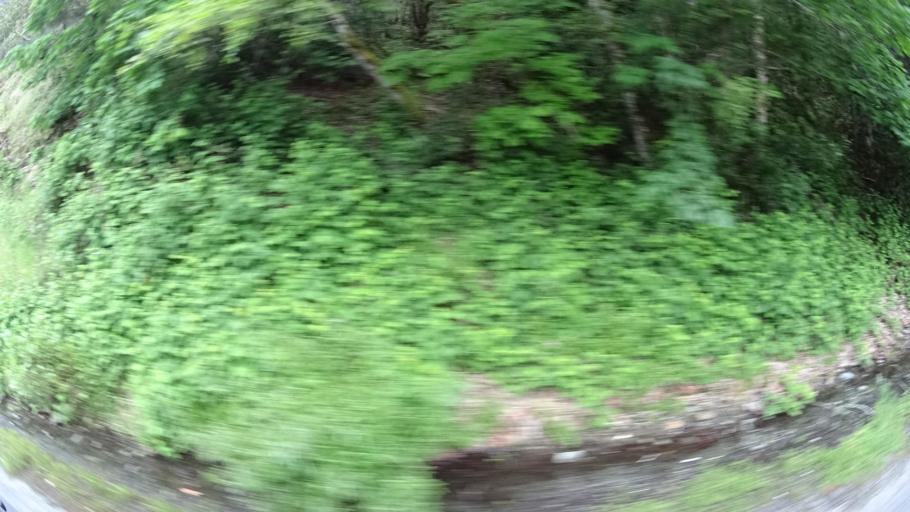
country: US
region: California
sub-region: Humboldt County
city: Willow Creek
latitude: 41.2754
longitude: -123.6077
